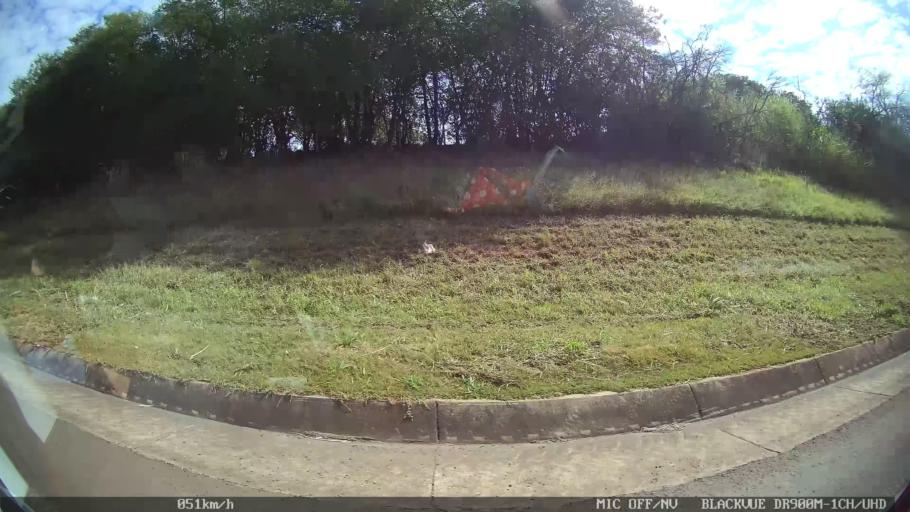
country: BR
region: Sao Paulo
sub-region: Santa Barbara D'Oeste
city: Santa Barbara d'Oeste
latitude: -22.7425
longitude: -47.4256
